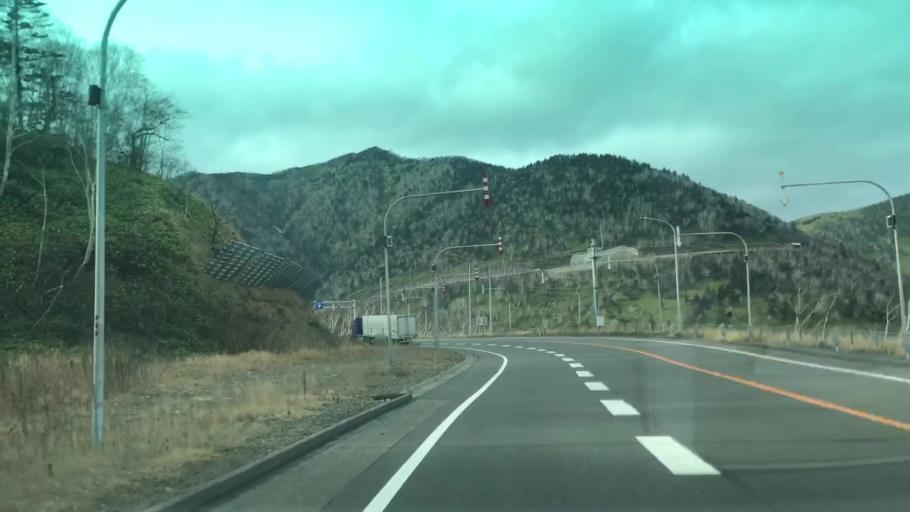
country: JP
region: Hokkaido
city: Otofuke
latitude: 42.9610
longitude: 142.7774
